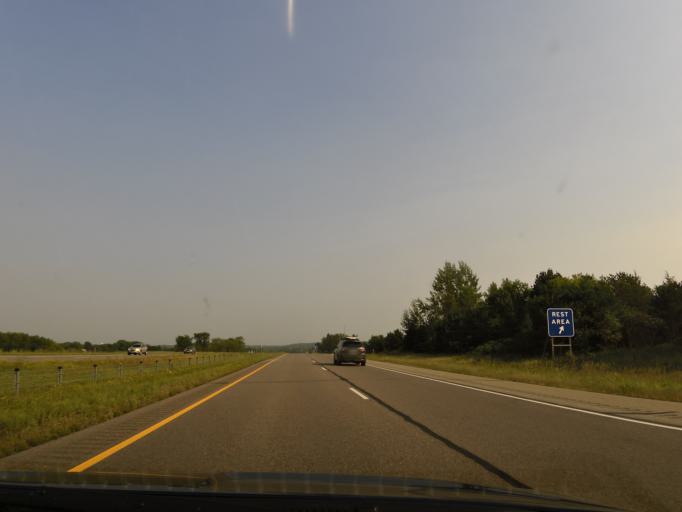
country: US
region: Minnesota
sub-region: Stearns County
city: Avon
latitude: 45.6072
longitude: -94.4905
